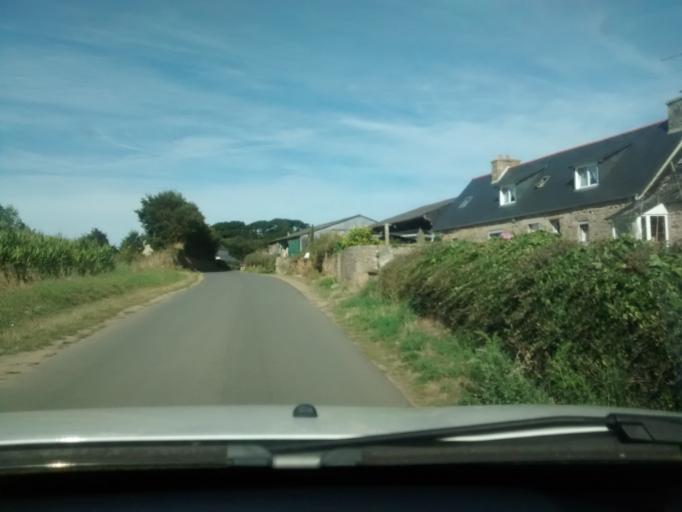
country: FR
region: Brittany
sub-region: Departement des Cotes-d'Armor
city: Plougrescant
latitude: 48.8645
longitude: -3.2228
